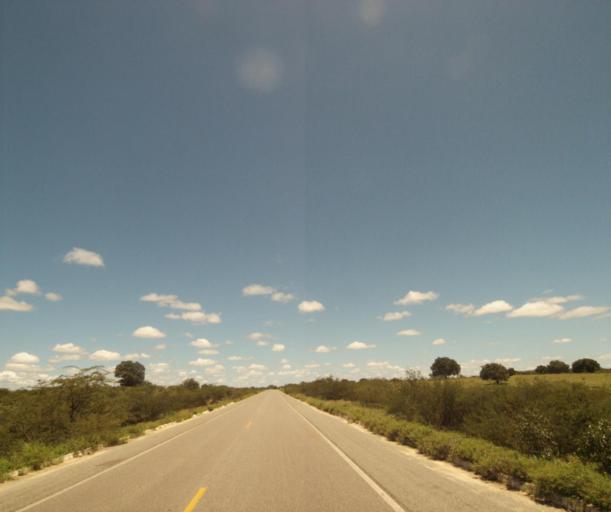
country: BR
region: Bahia
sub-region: Carinhanha
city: Carinhanha
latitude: -14.2956
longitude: -43.7855
